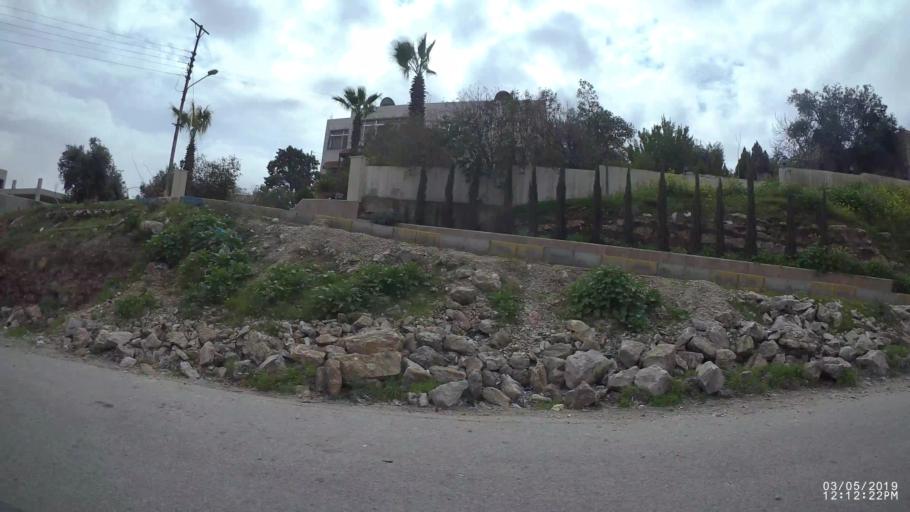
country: JO
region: Amman
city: Amman
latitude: 31.9914
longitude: 35.9371
